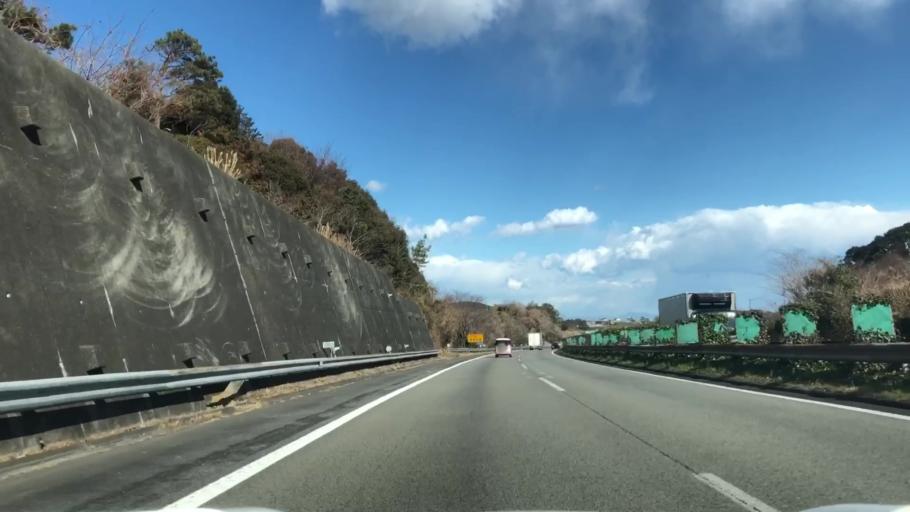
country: JP
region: Shizuoka
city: Shimada
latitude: 34.7688
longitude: 138.2189
